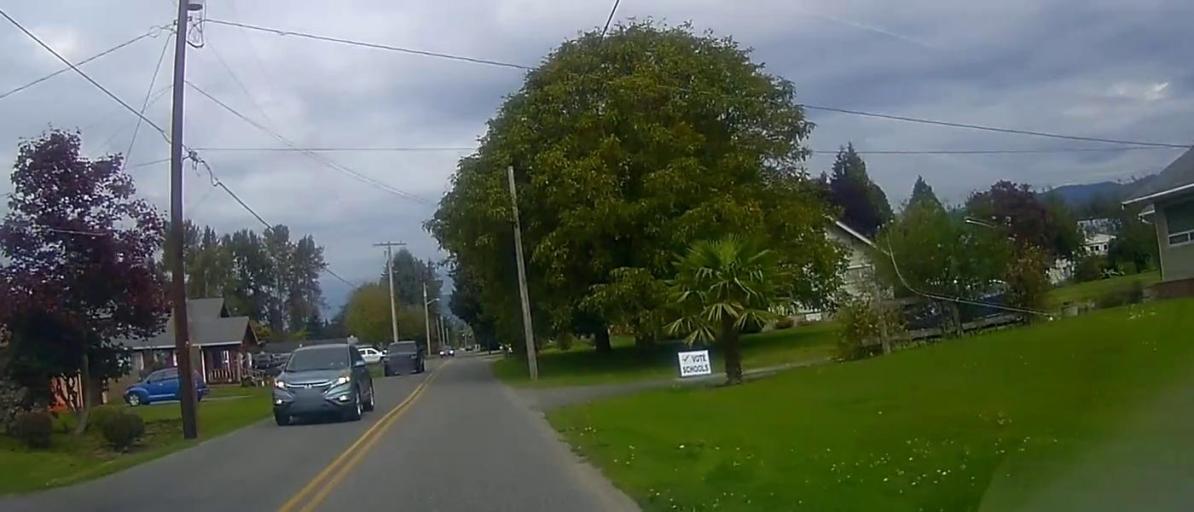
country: US
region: Washington
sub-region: Skagit County
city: Sedro-Woolley
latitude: 48.4977
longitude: -122.2584
